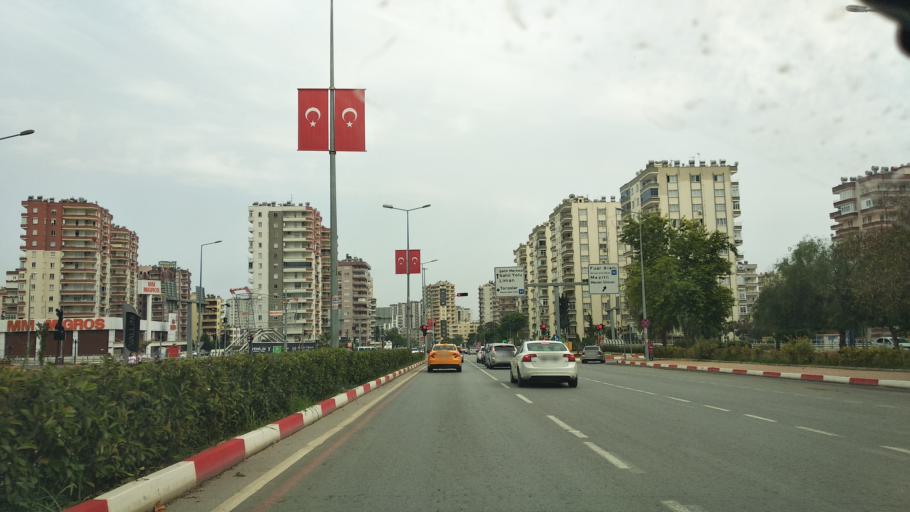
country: TR
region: Mersin
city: Mercin
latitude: 36.7955
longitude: 34.5972
